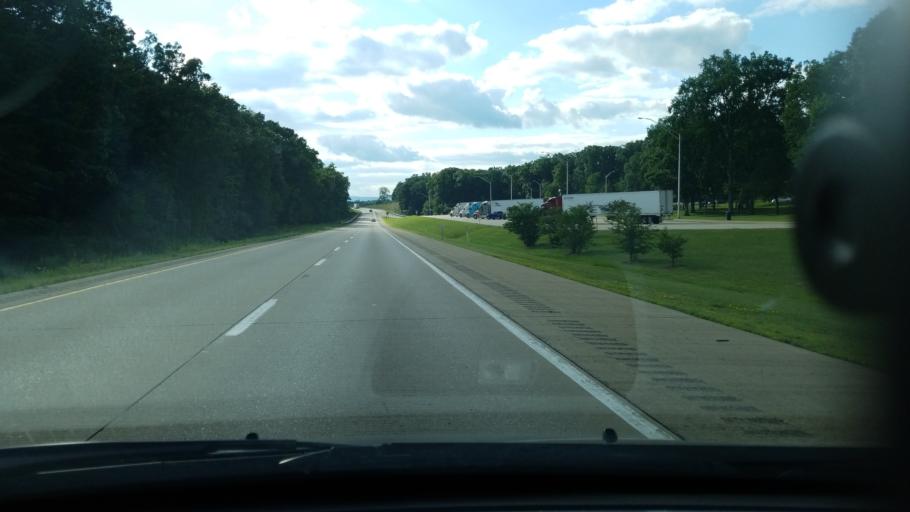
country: US
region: Pennsylvania
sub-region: Northumberland County
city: Riverside
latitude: 40.9891
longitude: -76.7243
